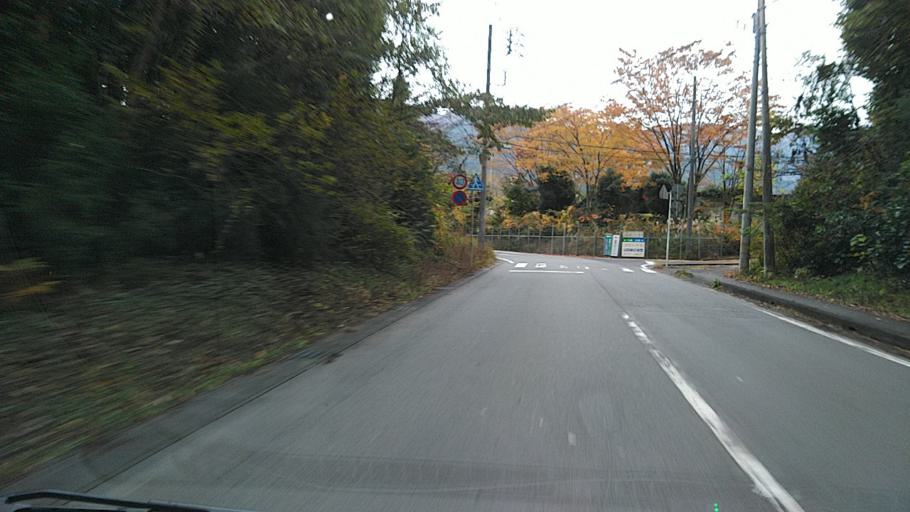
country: JP
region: Shizuoka
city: Gotemba
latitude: 35.3168
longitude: 138.9646
